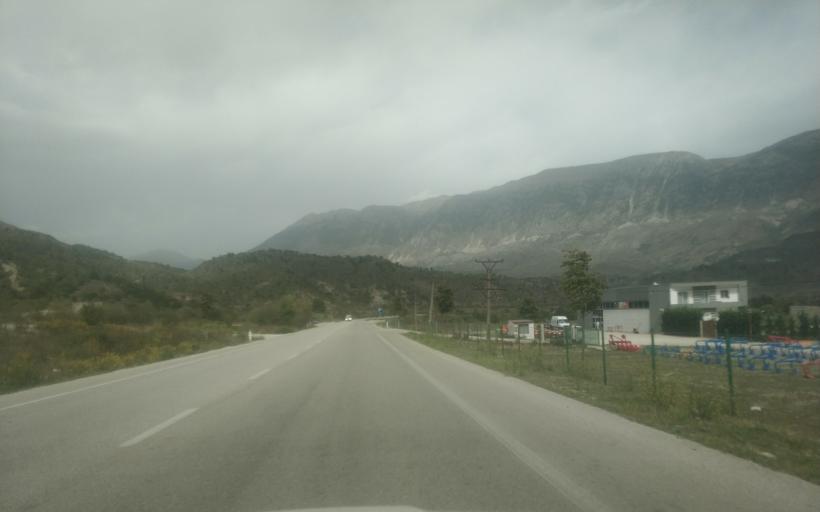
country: AL
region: Gjirokaster
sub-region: Rrethi i Gjirokastres
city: Picar
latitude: 40.1910
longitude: 20.0815
